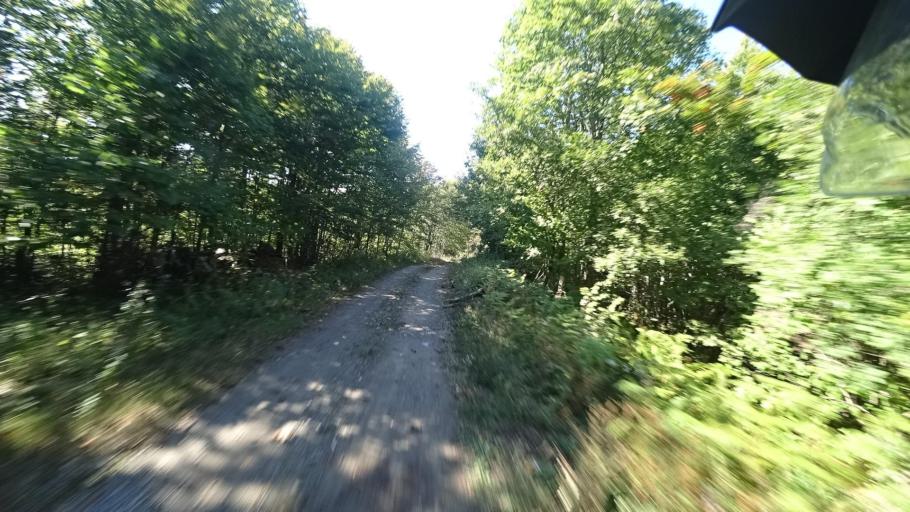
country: HR
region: Primorsko-Goranska
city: Vrbovsko
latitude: 45.2697
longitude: 15.1161
